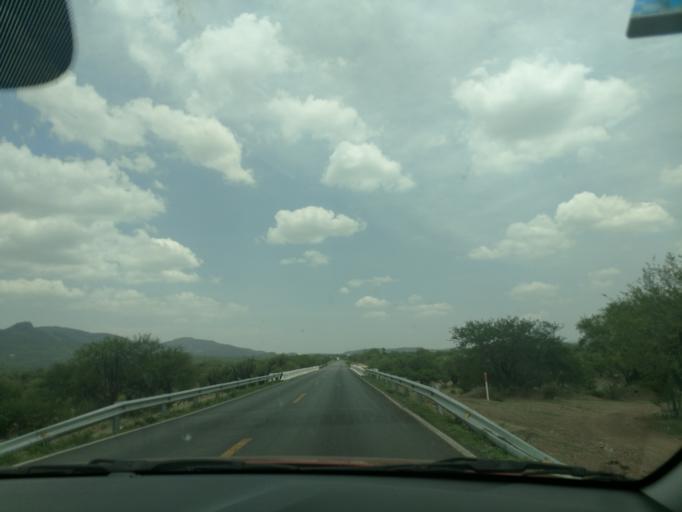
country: MX
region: San Luis Potosi
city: Villa Juarez
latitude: 22.0185
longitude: -100.3947
